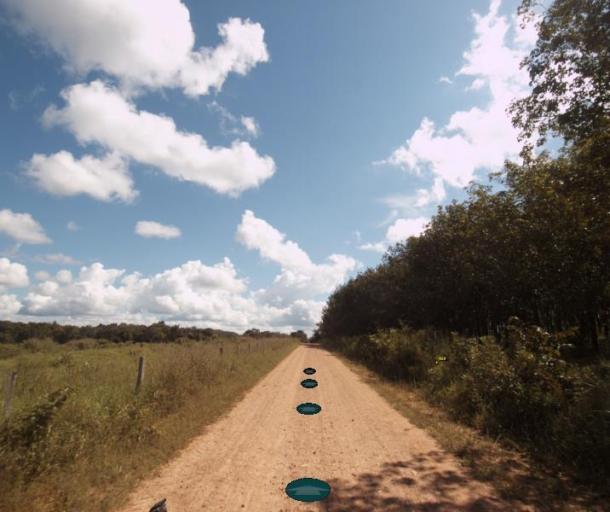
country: BR
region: Goias
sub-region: Pirenopolis
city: Pirenopolis
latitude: -15.7799
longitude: -49.0433
